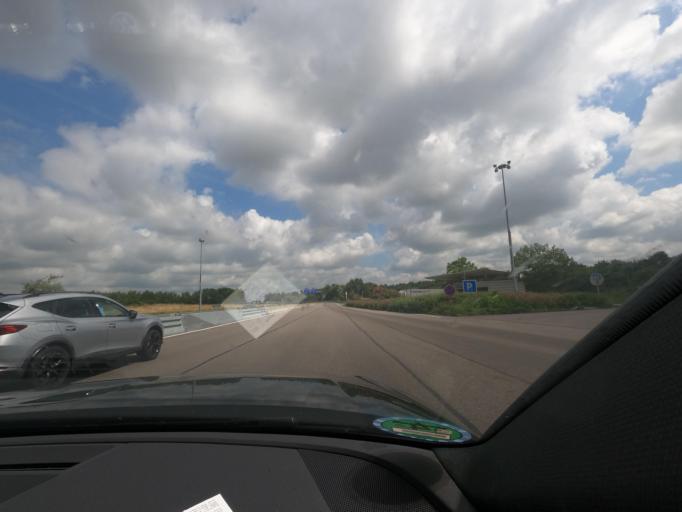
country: FR
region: Haute-Normandie
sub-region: Departement de la Seine-Maritime
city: Sainte-Marie-des-Champs
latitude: 49.6272
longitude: 0.8065
